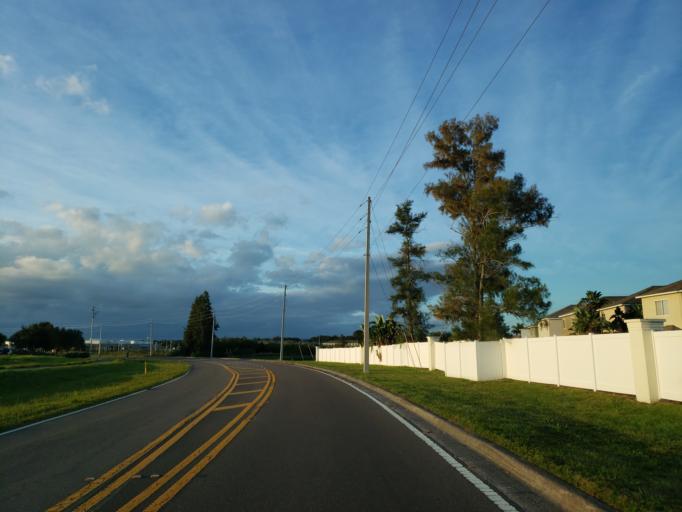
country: US
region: Florida
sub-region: Hillsborough County
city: Riverview
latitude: 27.7955
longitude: -82.3287
